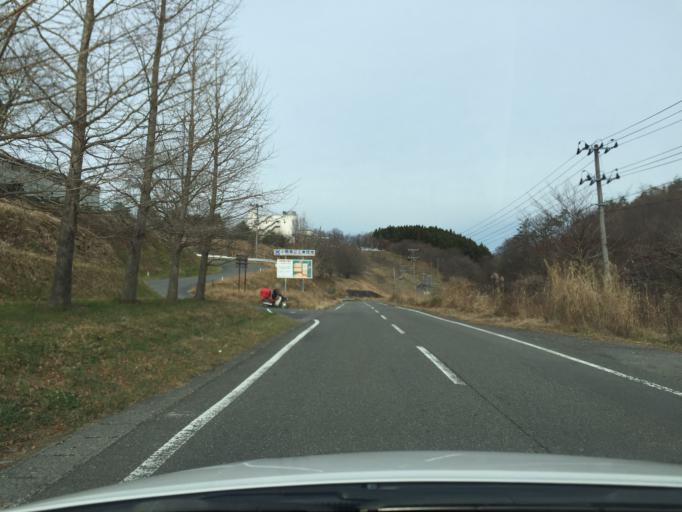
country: JP
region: Fukushima
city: Ishikawa
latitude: 37.2244
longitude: 140.6285
